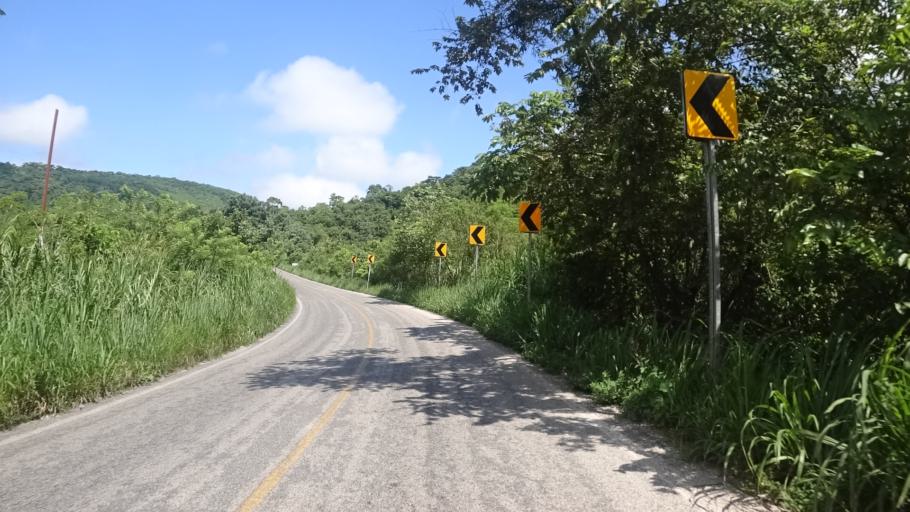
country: MX
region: Chiapas
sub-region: Palenque
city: Doctor Samuel Leon Brindis
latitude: 17.4534
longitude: -91.9631
